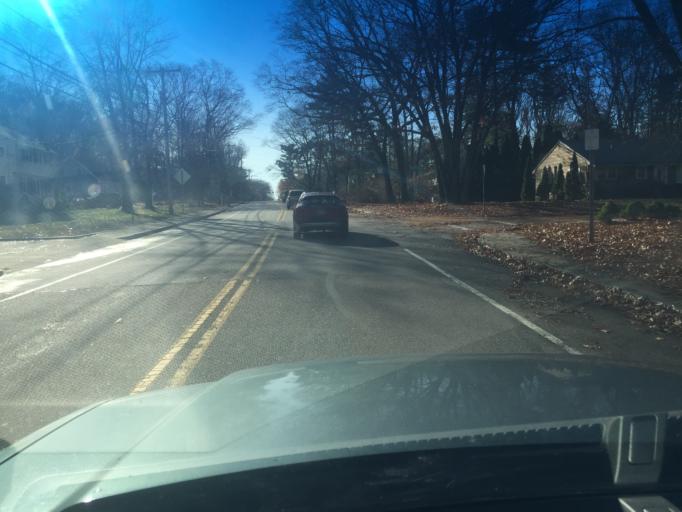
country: US
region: Massachusetts
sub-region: Norfolk County
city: Franklin
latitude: 42.1085
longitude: -71.4291
